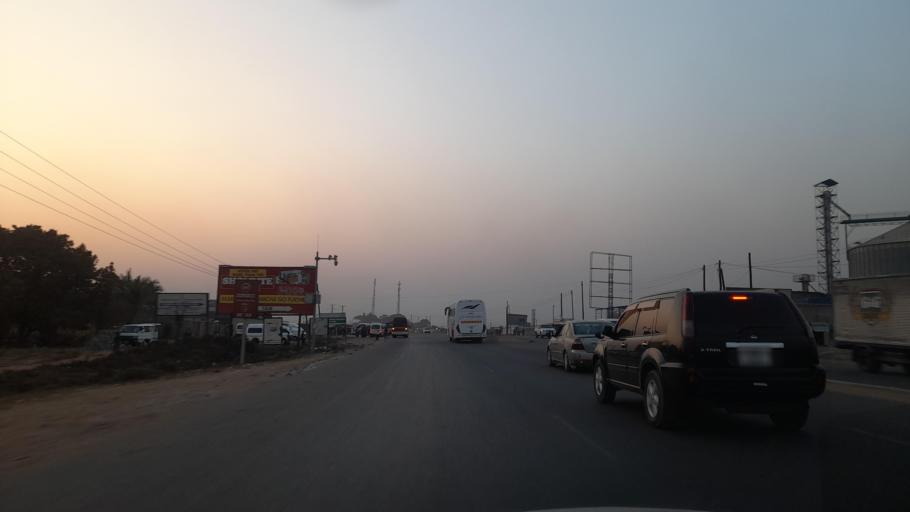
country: ZM
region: Copperbelt
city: Kitwe
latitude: -12.7776
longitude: 28.1935
